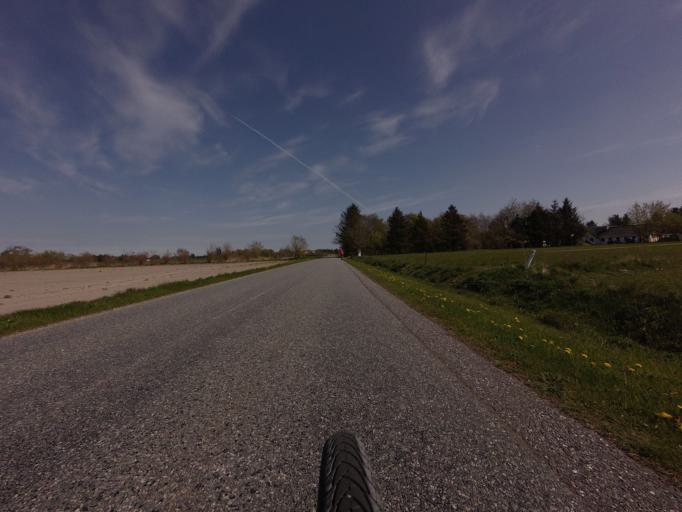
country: DK
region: North Denmark
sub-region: Jammerbugt Kommune
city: Pandrup
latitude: 57.2268
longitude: 9.6343
